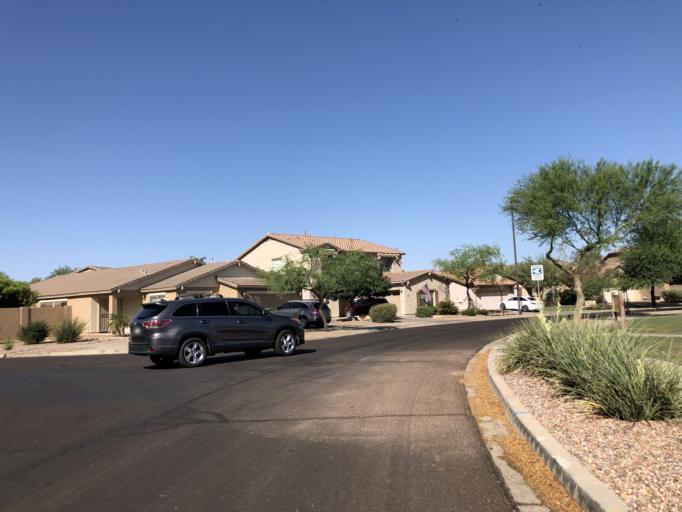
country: US
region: Arizona
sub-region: Maricopa County
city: Queen Creek
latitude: 33.2712
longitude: -111.7021
